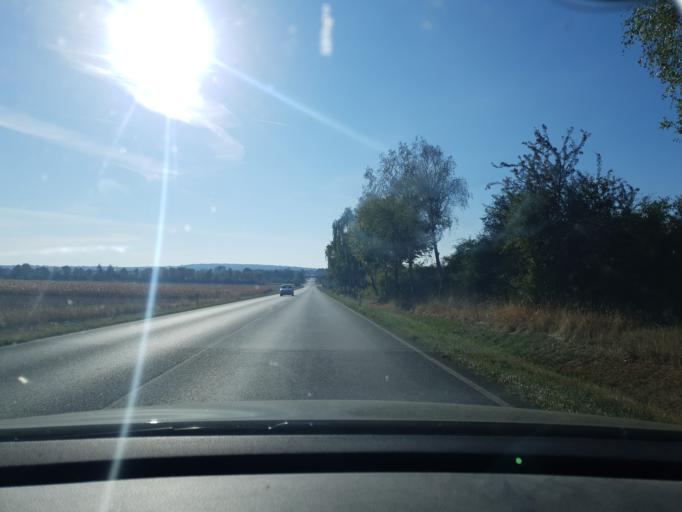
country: DE
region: Hesse
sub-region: Regierungsbezirk Giessen
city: Langgons
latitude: 50.4687
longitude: 8.6341
